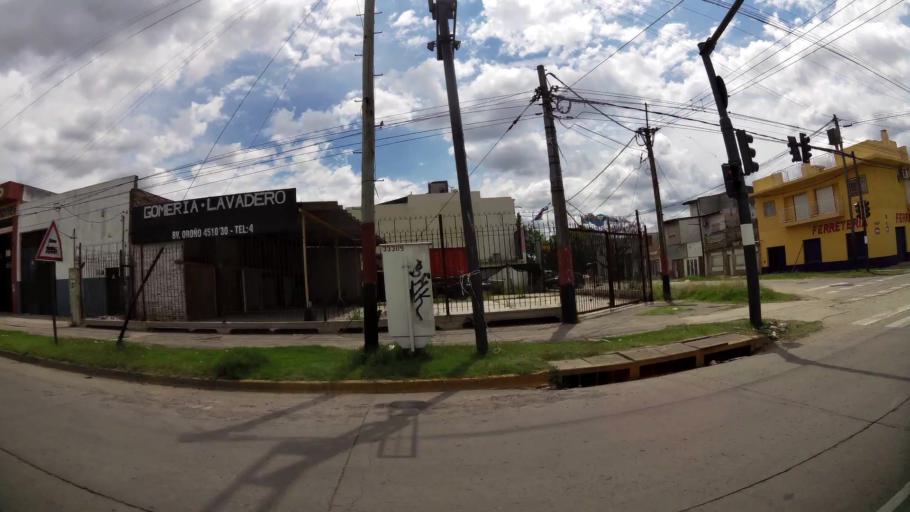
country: AR
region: Santa Fe
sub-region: Departamento de Rosario
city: Rosario
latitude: -32.9869
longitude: -60.6642
